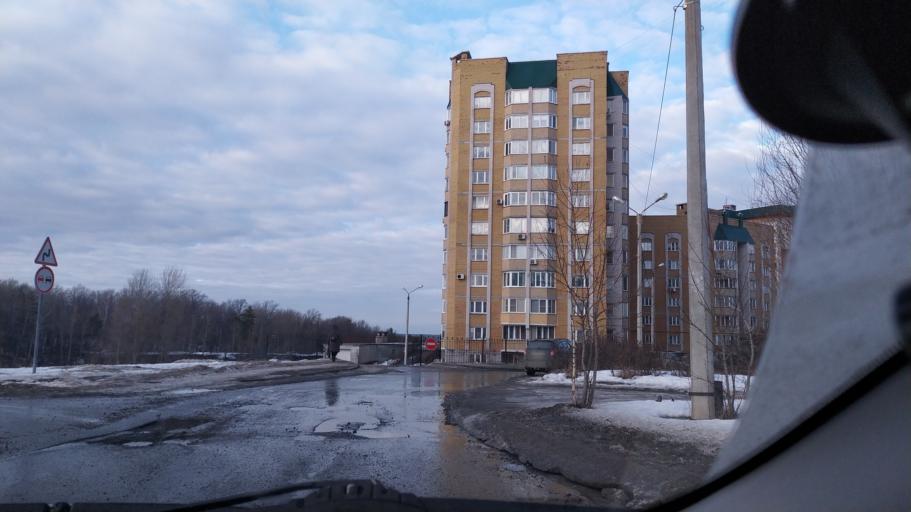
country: RU
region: Chuvashia
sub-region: Cheboksarskiy Rayon
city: Cheboksary
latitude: 56.1485
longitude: 47.2139
